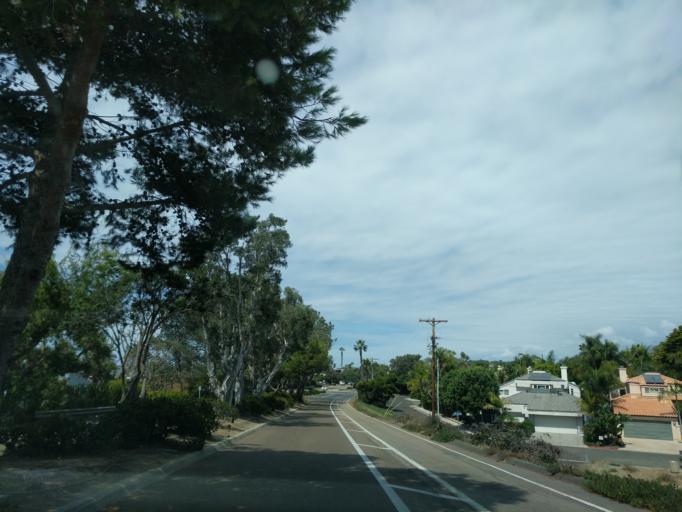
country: US
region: California
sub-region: San Diego County
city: Del Mar
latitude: 32.9667
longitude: -117.2664
